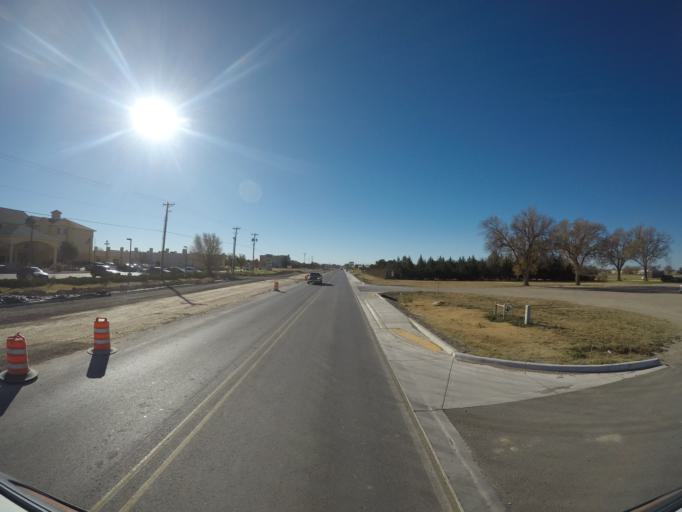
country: US
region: New Mexico
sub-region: Curry County
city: Clovis
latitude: 34.4441
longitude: -103.1965
